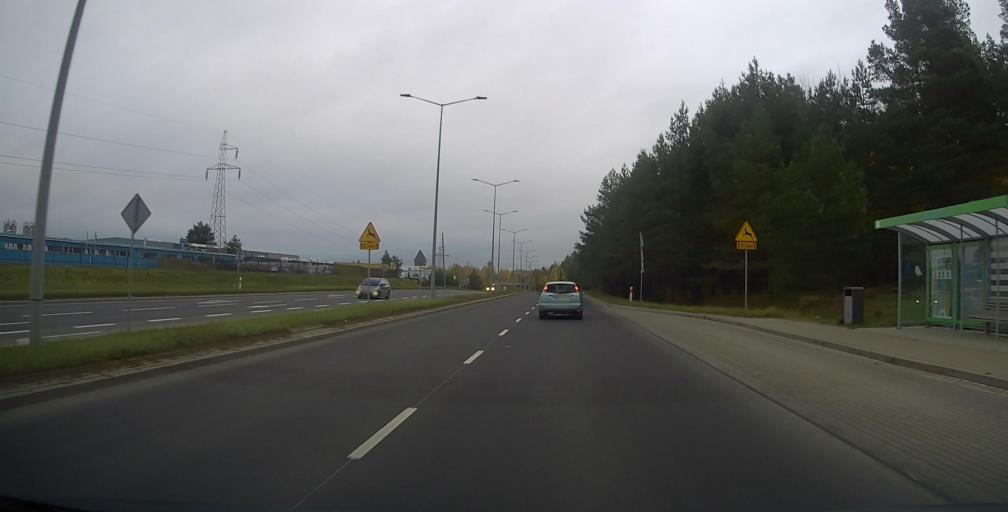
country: PL
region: Warmian-Masurian Voivodeship
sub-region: Powiat elcki
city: Elk
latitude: 53.8148
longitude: 22.3840
